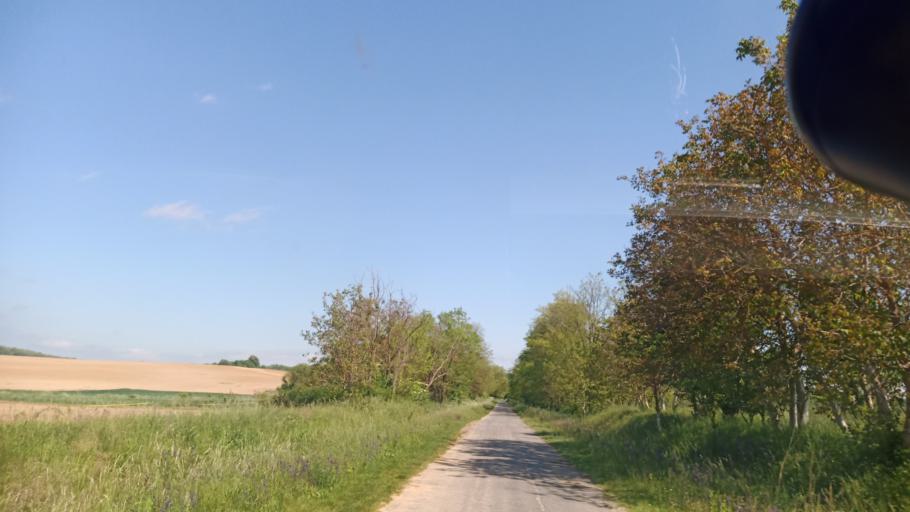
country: HU
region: Zala
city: Pacsa
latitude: 46.6371
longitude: 17.0620
